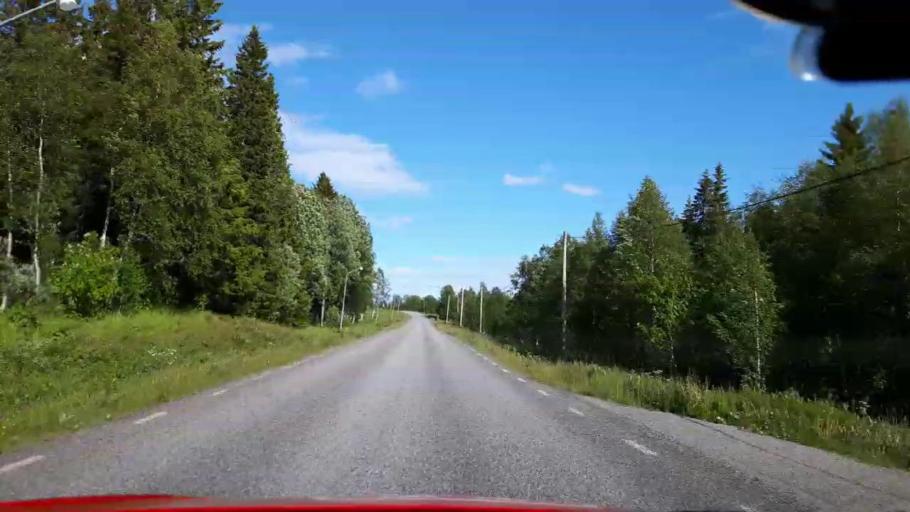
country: SE
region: Jaemtland
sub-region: Krokoms Kommun
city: Valla
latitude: 63.6994
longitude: 14.1573
